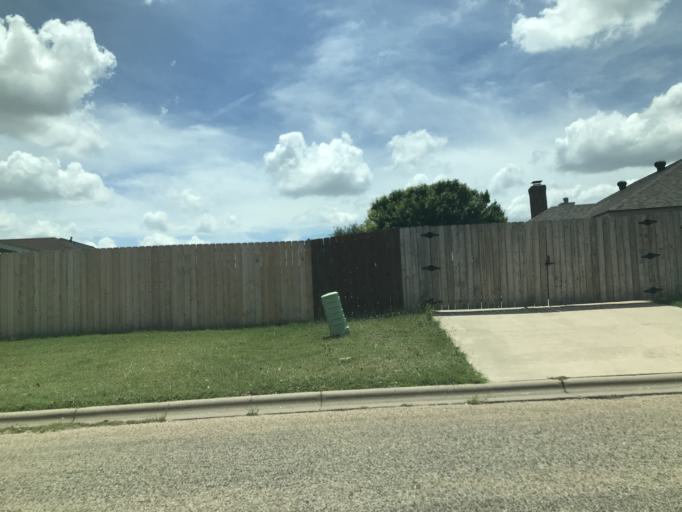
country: US
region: Texas
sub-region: Taylor County
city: Abilene
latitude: 32.4863
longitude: -99.6858
